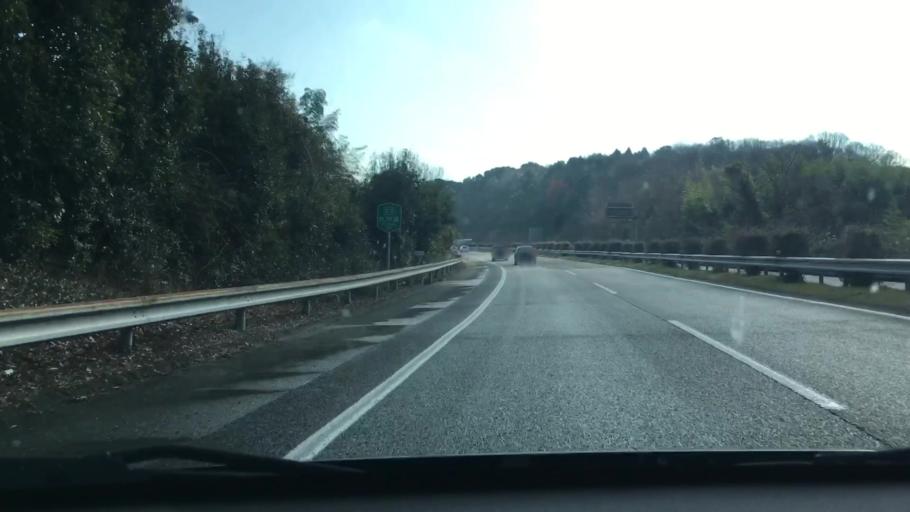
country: JP
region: Kumamoto
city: Matsubase
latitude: 32.6441
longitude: 130.7067
